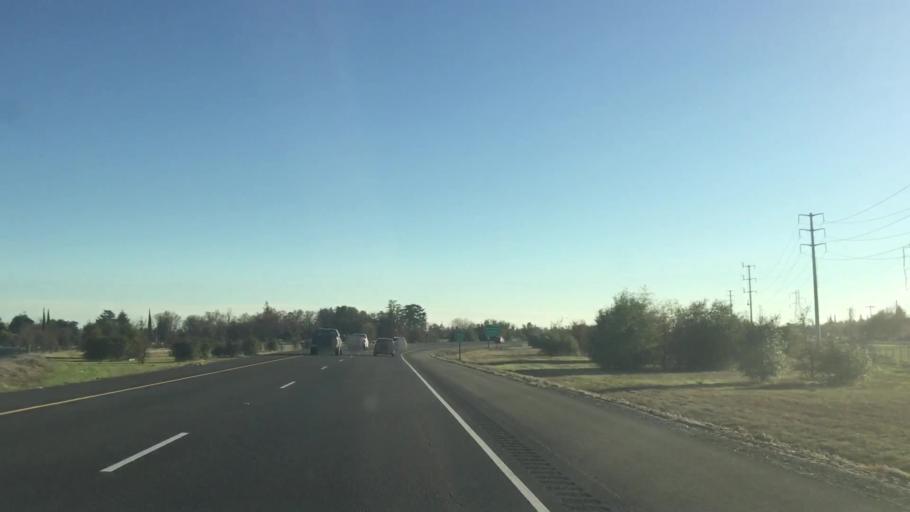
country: US
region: California
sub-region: Yuba County
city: Olivehurst
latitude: 39.0921
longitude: -121.5418
